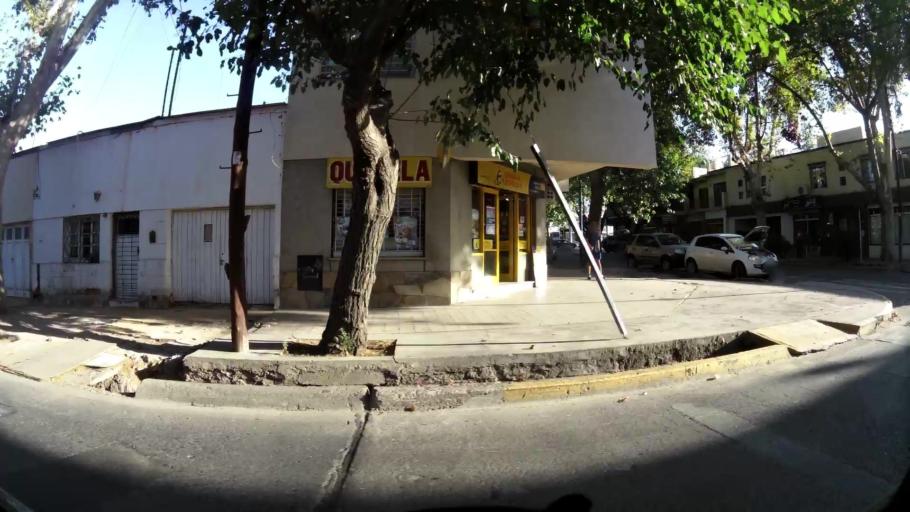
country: AR
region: Mendoza
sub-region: Departamento de Godoy Cruz
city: Godoy Cruz
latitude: -32.9077
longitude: -68.8515
